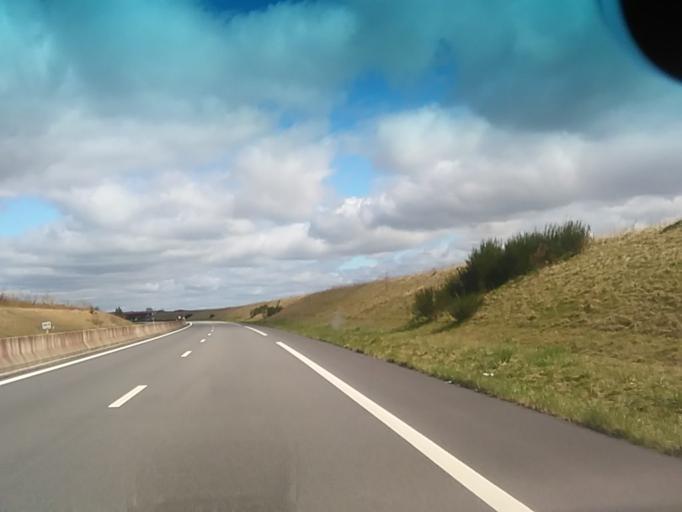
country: FR
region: Haute-Normandie
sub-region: Departement de l'Eure
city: Brionne
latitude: 49.1862
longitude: 0.7641
